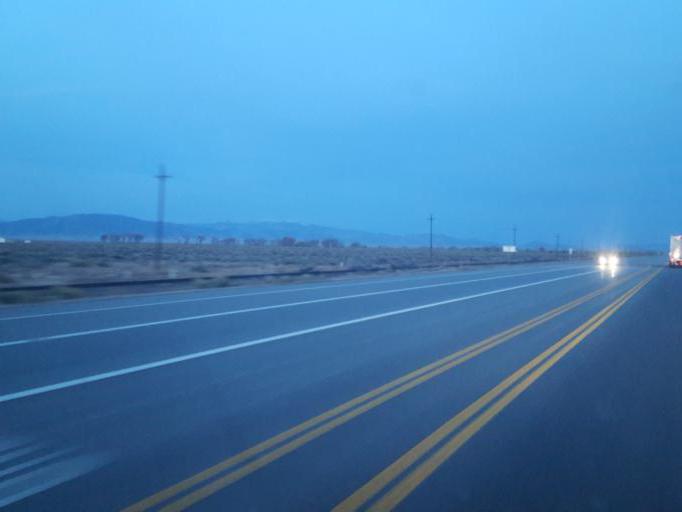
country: US
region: Colorado
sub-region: Alamosa County
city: Alamosa
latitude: 37.5133
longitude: -105.9844
